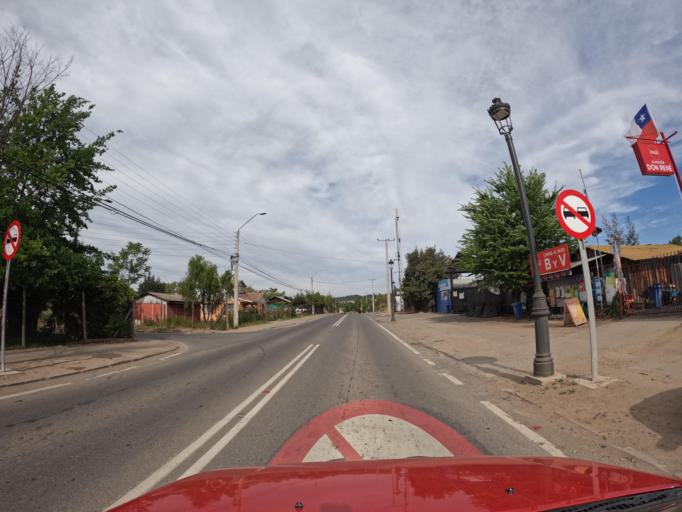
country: CL
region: Maule
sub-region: Provincia de Talca
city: Talca
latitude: -35.3933
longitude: -71.8062
